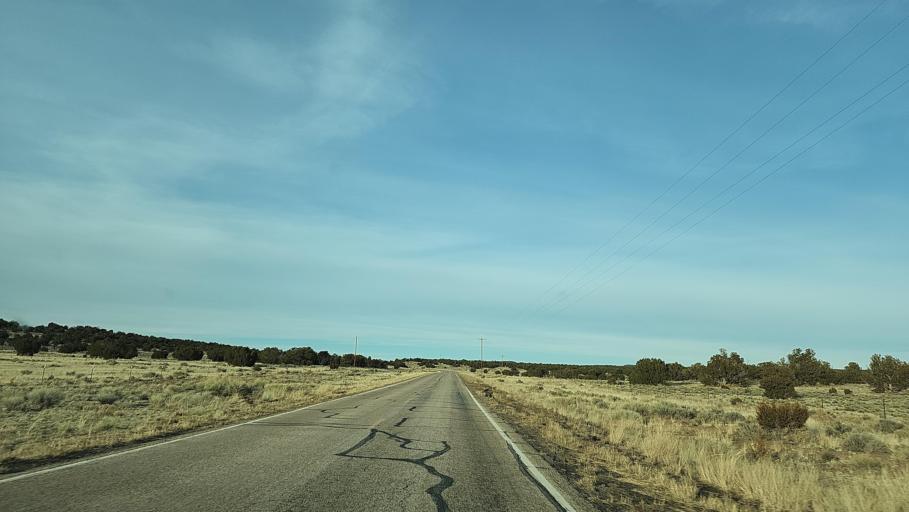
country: US
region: New Mexico
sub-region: Catron County
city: Reserve
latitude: 34.4019
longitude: -108.4405
